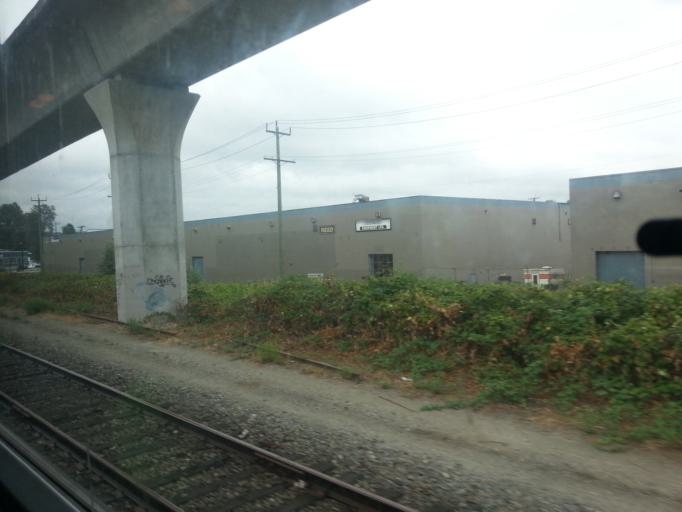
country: CA
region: British Columbia
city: New Westminster
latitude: 49.2232
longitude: -122.8912
